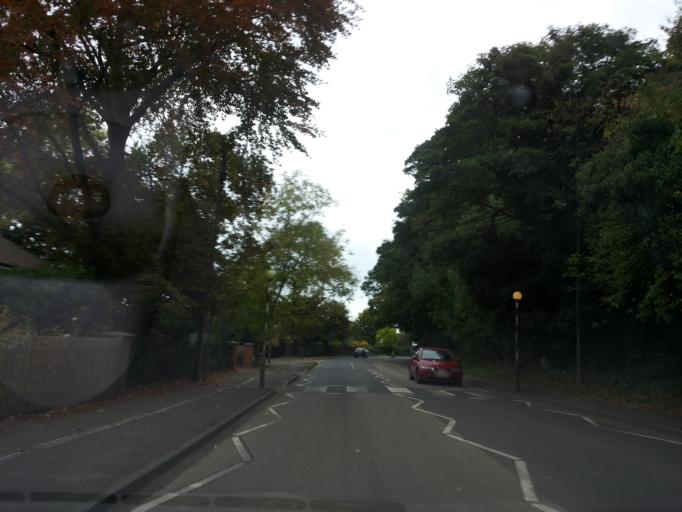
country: GB
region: England
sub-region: Buckinghamshire
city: Little Chalfont
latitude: 51.6683
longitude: -0.5698
